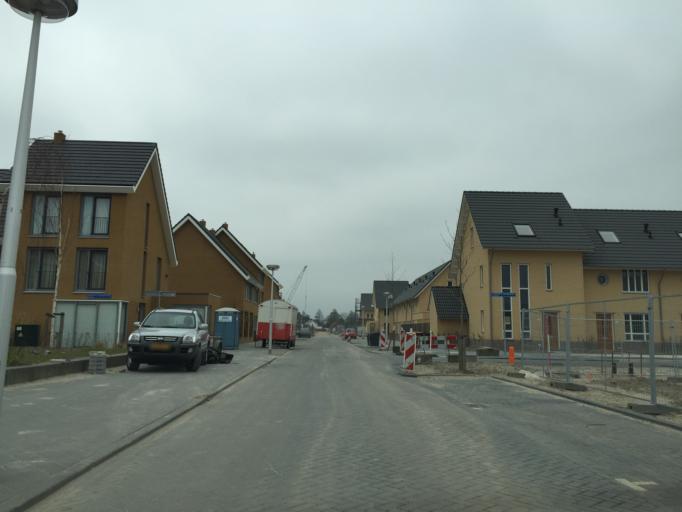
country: NL
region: Utrecht
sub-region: Stichtse Vecht
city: Maarssen
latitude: 52.0963
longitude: 5.0522
